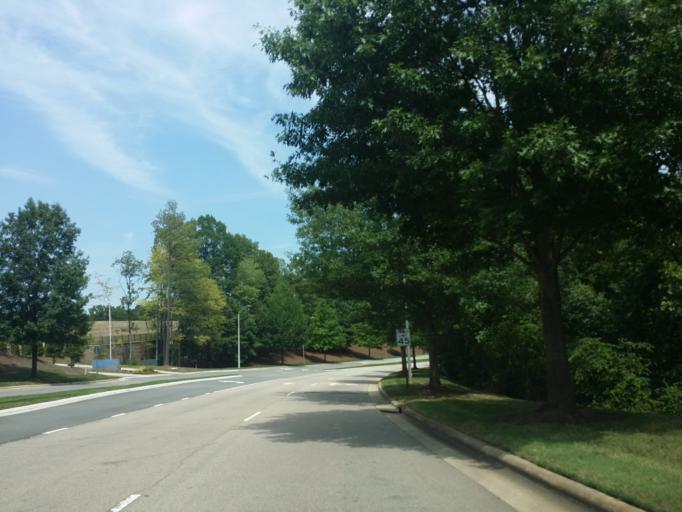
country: US
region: North Carolina
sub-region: Wake County
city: Morrisville
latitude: 35.8285
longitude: -78.7982
